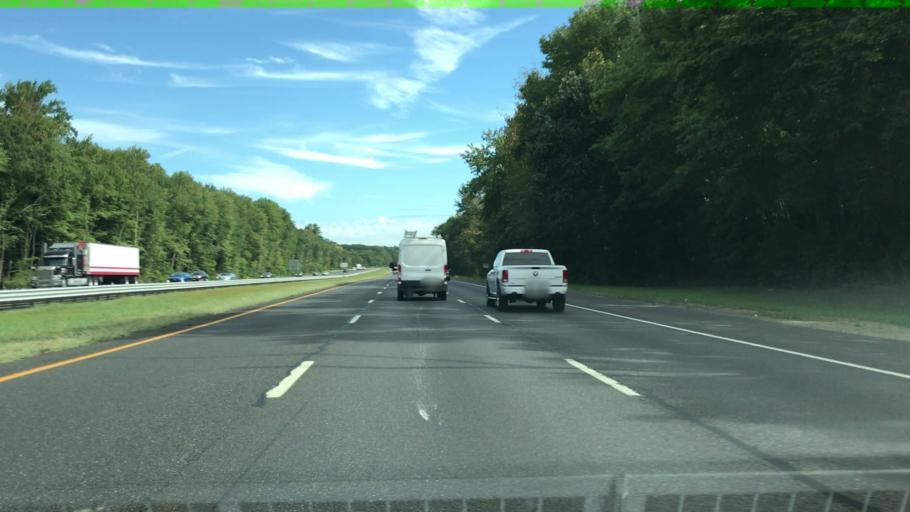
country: US
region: New Jersey
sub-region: Burlington County
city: Burlington
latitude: 40.0545
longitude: -74.8210
